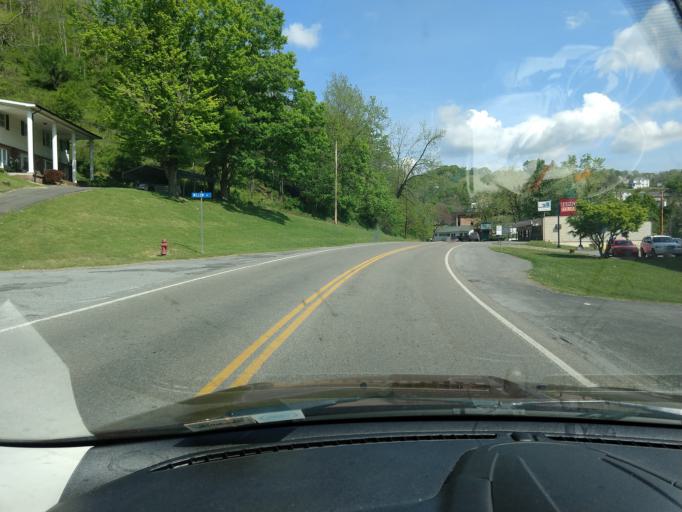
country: US
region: Virginia
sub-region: Russell County
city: Honaker
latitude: 37.0142
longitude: -81.9696
